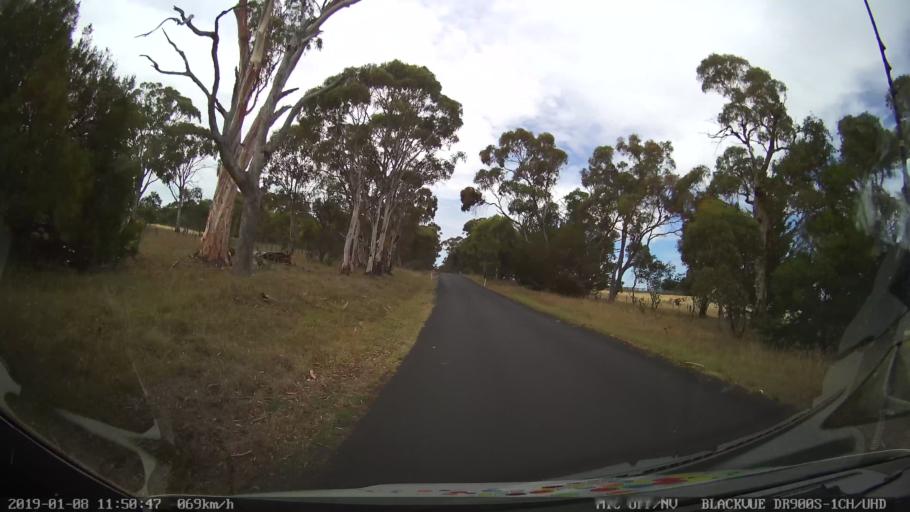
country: AU
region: New South Wales
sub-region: Armidale Dumaresq
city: Armidale
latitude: -30.3864
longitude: 151.5575
